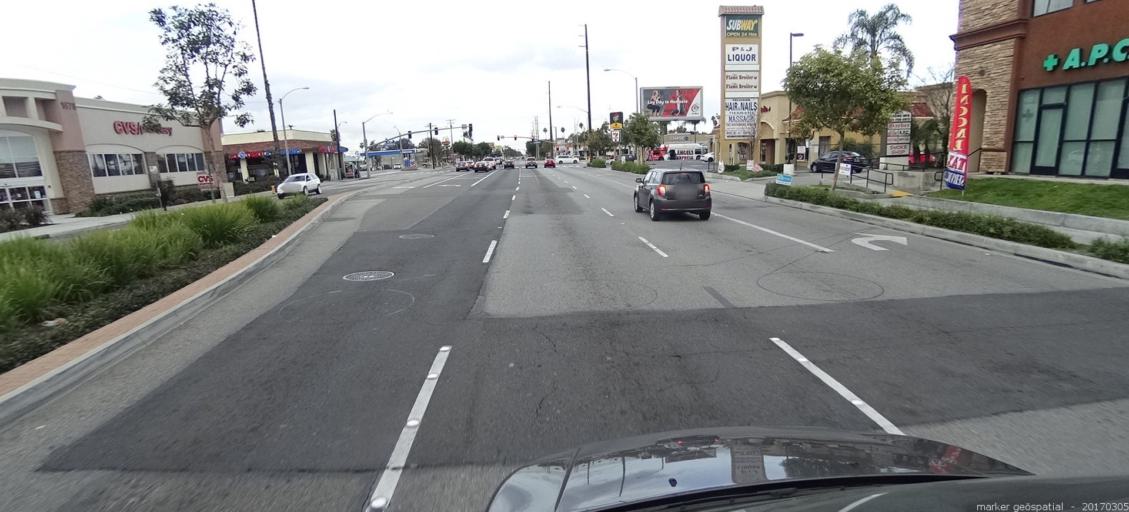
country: US
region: California
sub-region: Orange County
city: Garden Grove
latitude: 33.8032
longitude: -117.9400
